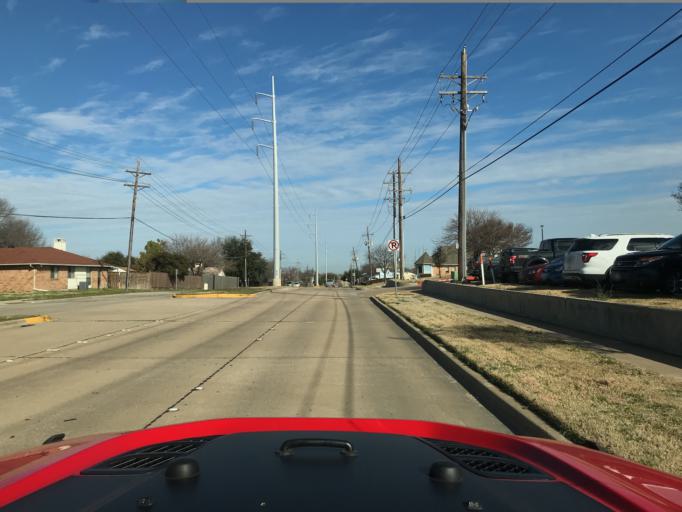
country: US
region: Texas
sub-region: Denton County
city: Lewisville
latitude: 33.0442
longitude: -97.0359
